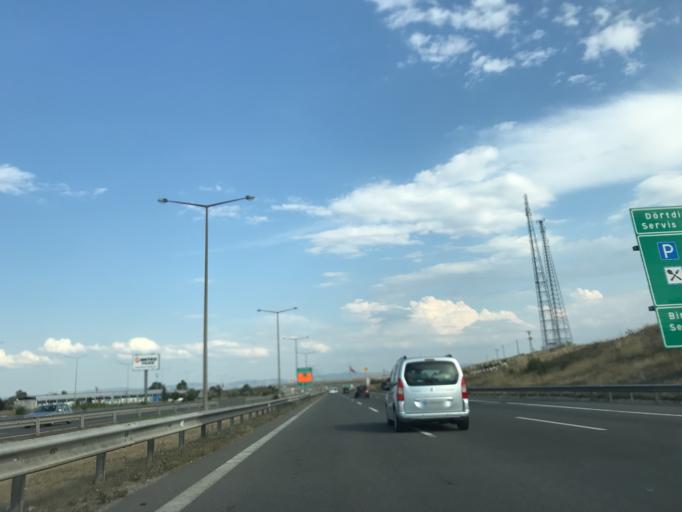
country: TR
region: Bolu
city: Dortdivan
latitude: 40.7530
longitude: 32.0750
